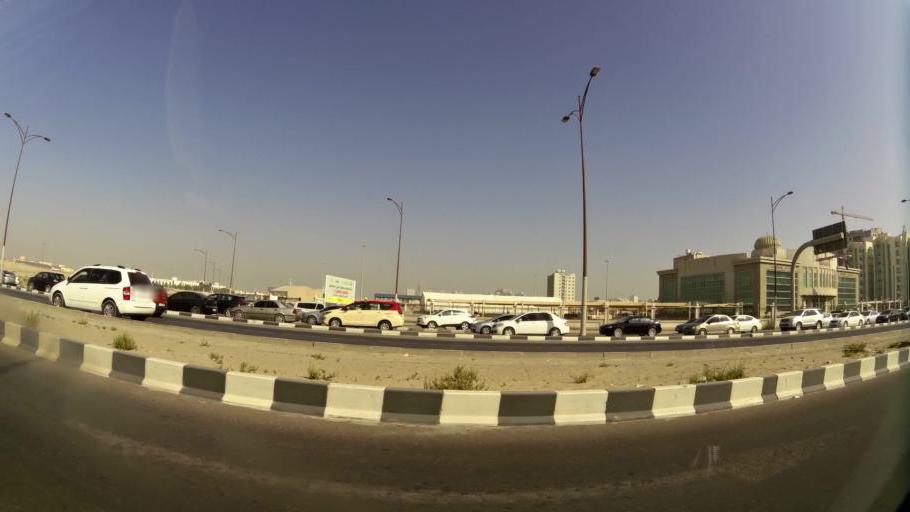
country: AE
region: Ajman
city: Ajman
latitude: 25.3748
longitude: 55.4570
